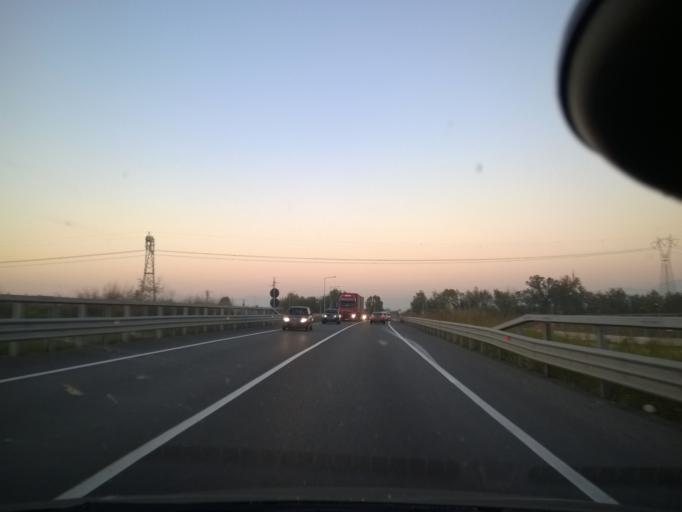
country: IT
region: Lombardy
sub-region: Provincia di Brescia
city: Travagliato
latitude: 45.5319
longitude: 10.0548
